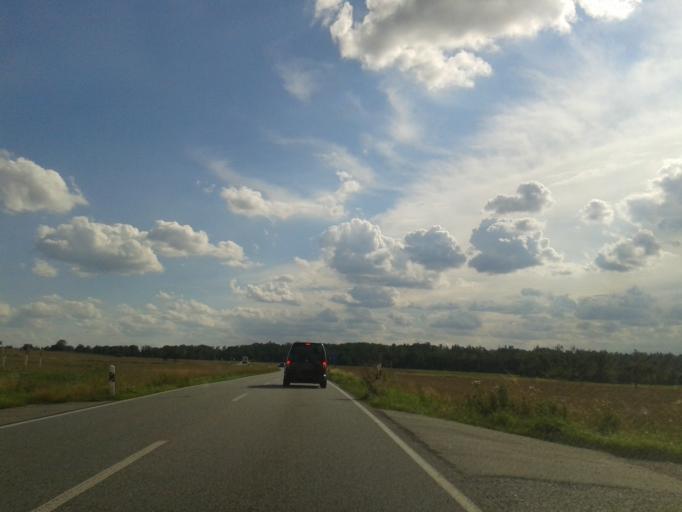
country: DE
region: Saxony
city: Lichtenberg
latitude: 51.1451
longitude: 13.9564
